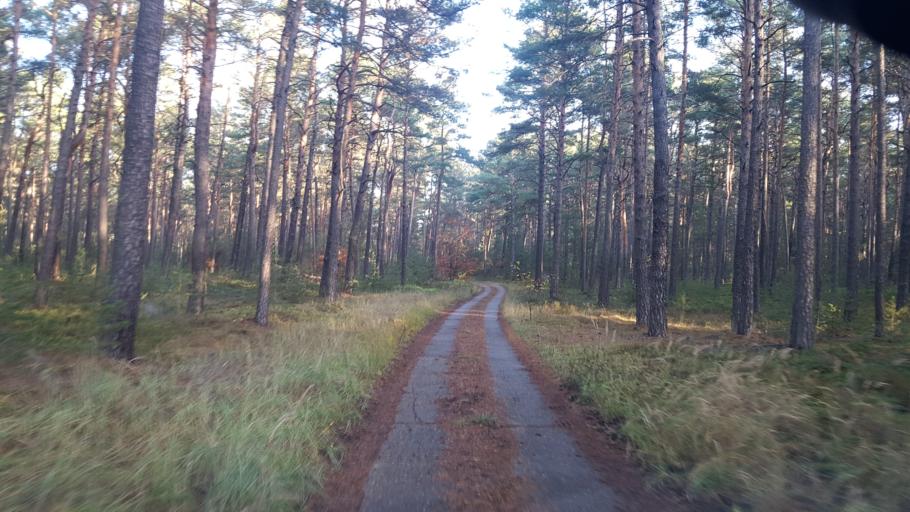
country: DE
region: Brandenburg
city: Crinitz
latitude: 51.7130
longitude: 13.7424
